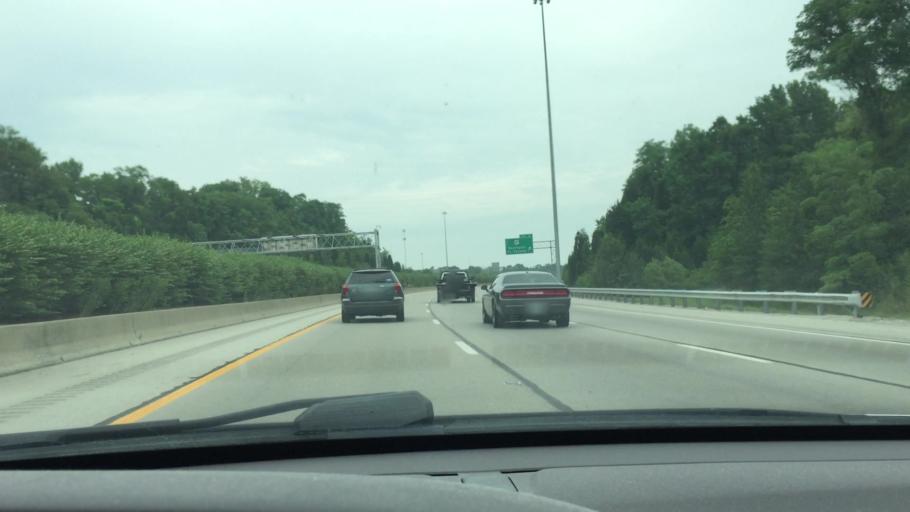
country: US
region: Kentucky
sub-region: Campbell County
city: Southgate
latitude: 39.0615
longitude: -84.4688
